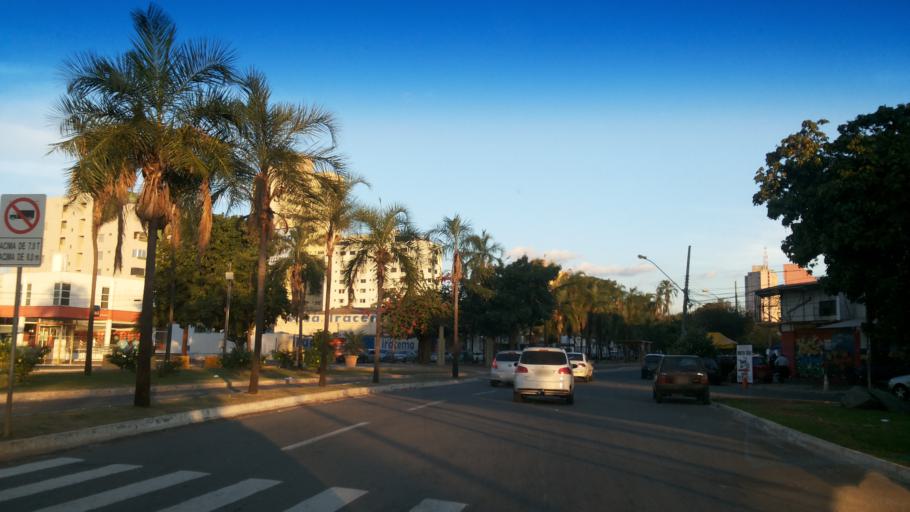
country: BR
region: Goias
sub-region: Goiania
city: Goiania
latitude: -16.6645
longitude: -49.2617
